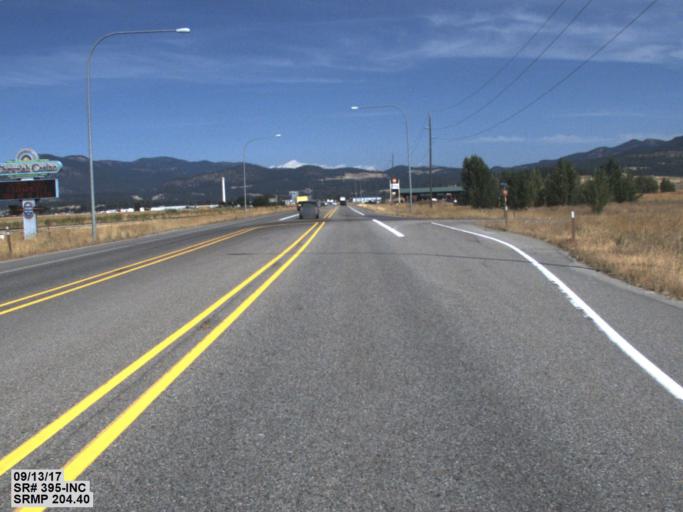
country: US
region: Washington
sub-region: Stevens County
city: Chewelah
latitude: 48.2365
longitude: -117.7152
